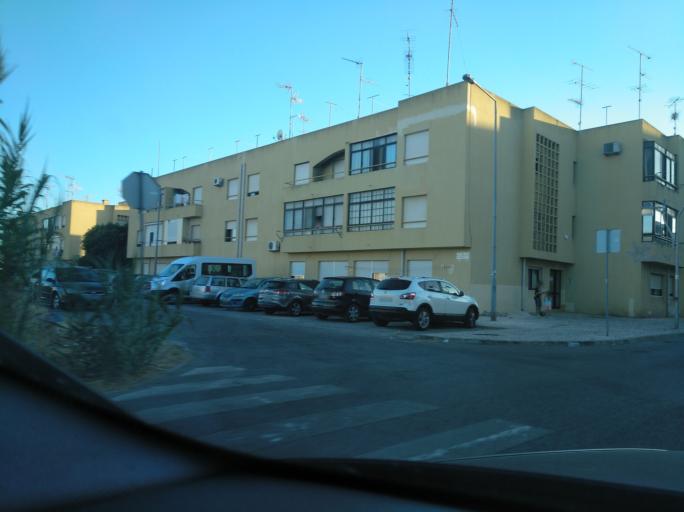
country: PT
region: Faro
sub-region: Vila Real de Santo Antonio
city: Vila Real de Santo Antonio
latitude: 37.1970
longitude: -7.4247
